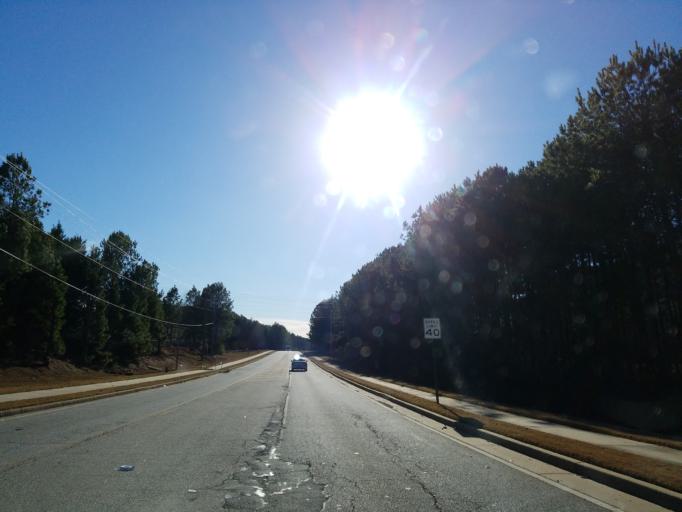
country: US
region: Georgia
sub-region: Cobb County
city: Mableton
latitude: 33.7973
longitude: -84.5157
